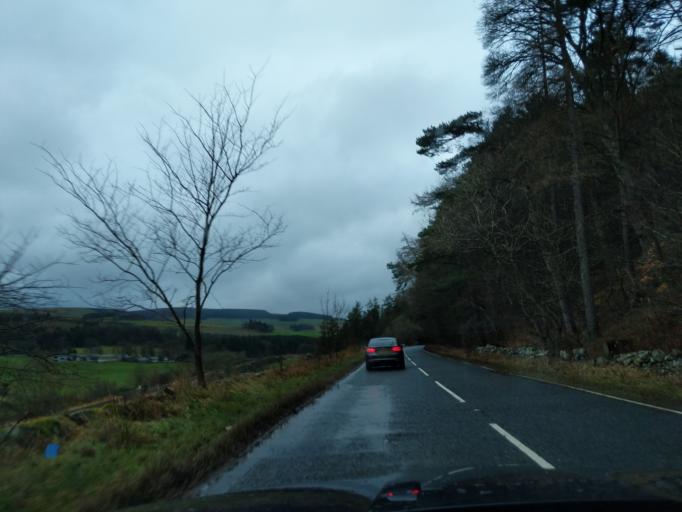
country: GB
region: Scotland
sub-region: The Scottish Borders
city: Galashiels
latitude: 55.6474
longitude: -2.8578
